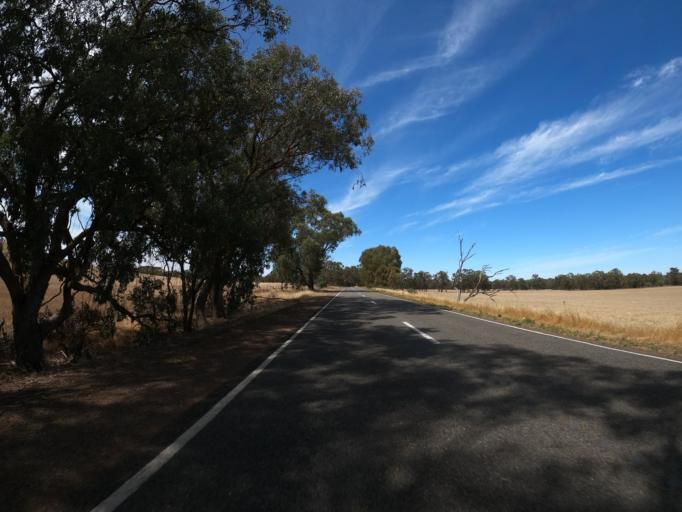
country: AU
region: Victoria
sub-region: Benalla
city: Benalla
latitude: -36.3403
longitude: 145.9590
